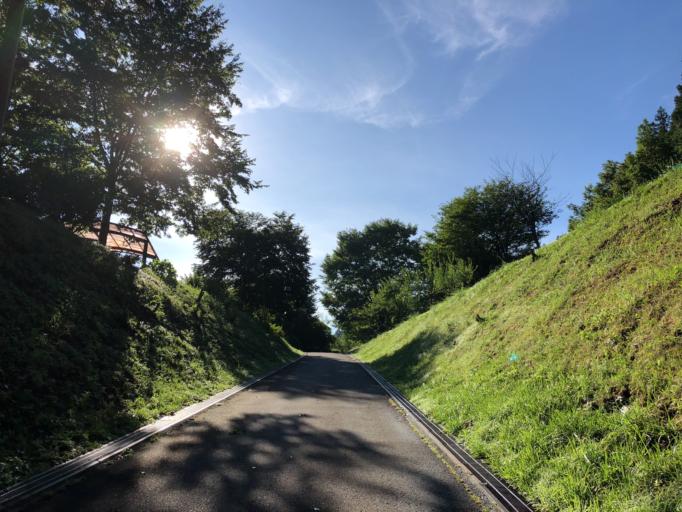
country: JP
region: Yamanashi
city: Uenohara
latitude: 35.6800
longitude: 139.0659
